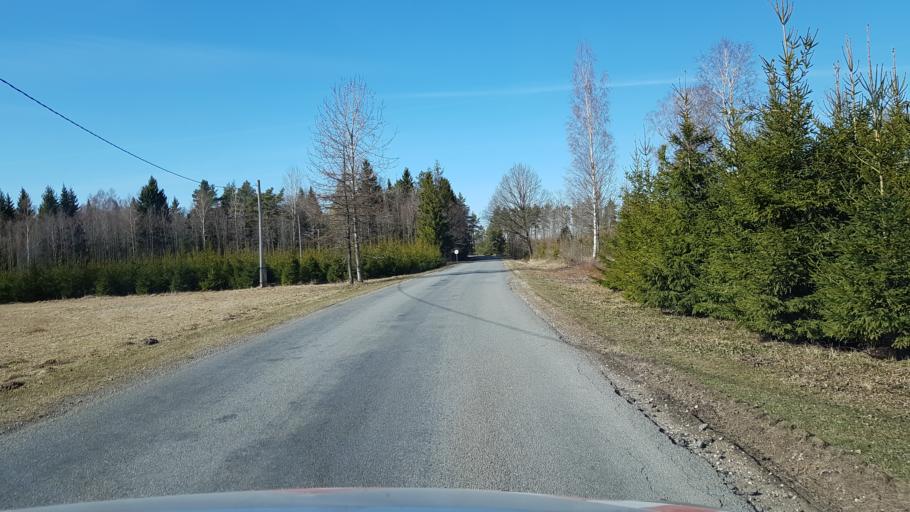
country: EE
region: Harju
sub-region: Nissi vald
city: Riisipere
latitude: 59.0933
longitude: 24.3423
